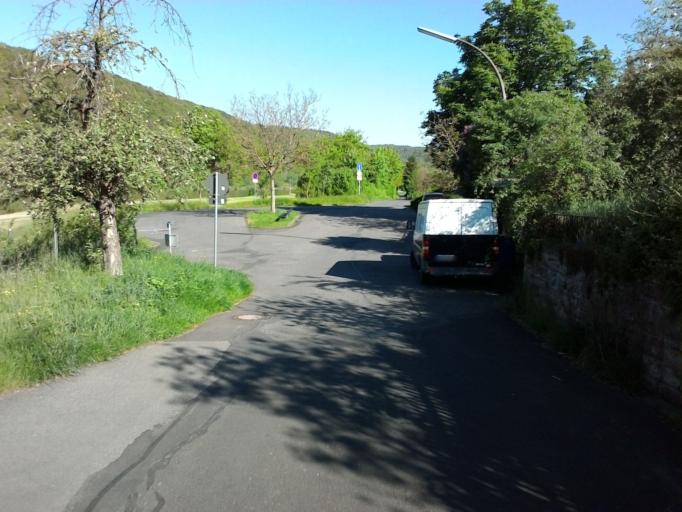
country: DE
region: Bavaria
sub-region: Regierungsbezirk Unterfranken
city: Rothenfels
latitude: 49.8931
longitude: 9.5947
